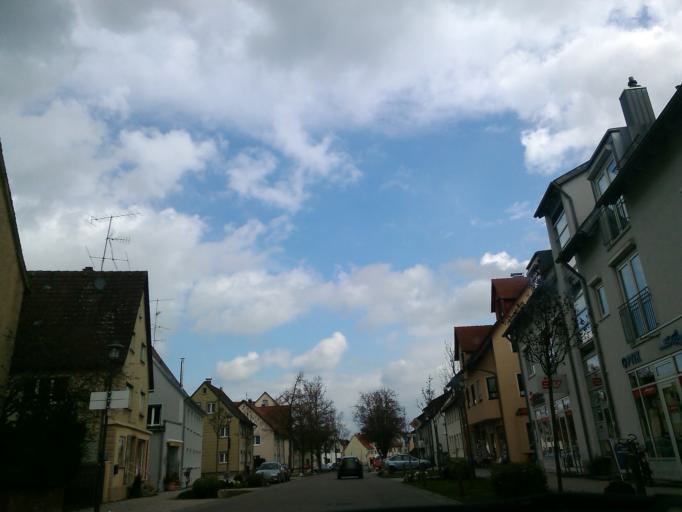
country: DE
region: Baden-Wuerttemberg
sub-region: Tuebingen Region
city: Langenau
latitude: 48.5000
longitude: 10.1216
